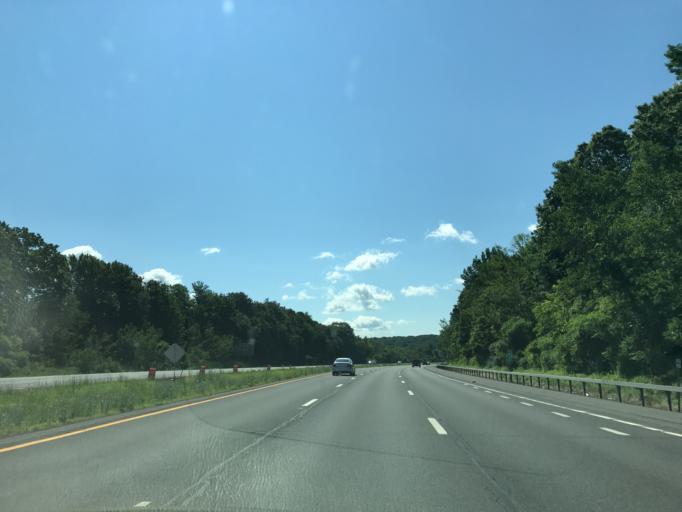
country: US
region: New York
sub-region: Rensselaer County
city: Hampton Manor
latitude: 42.6262
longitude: -73.6982
